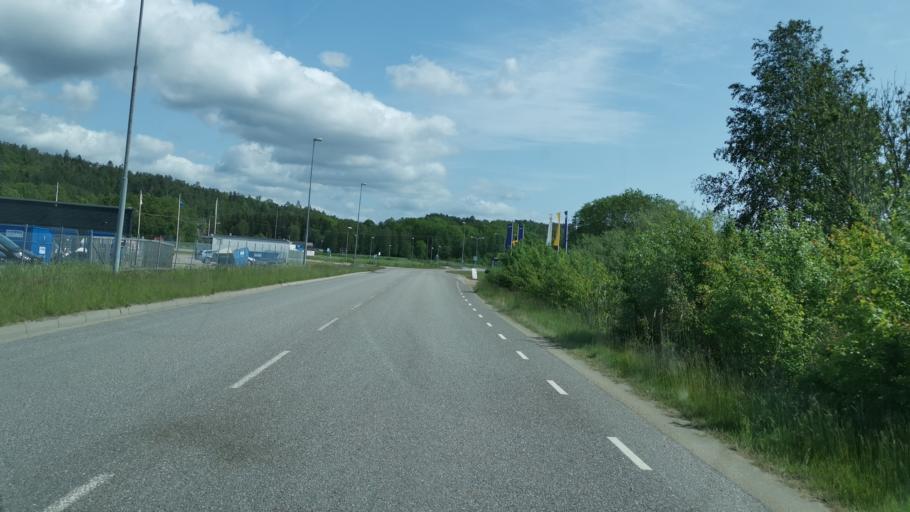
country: SE
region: Vaestra Goetaland
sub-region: Uddevalla Kommun
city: Uddevalla
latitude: 58.3495
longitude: 11.8666
